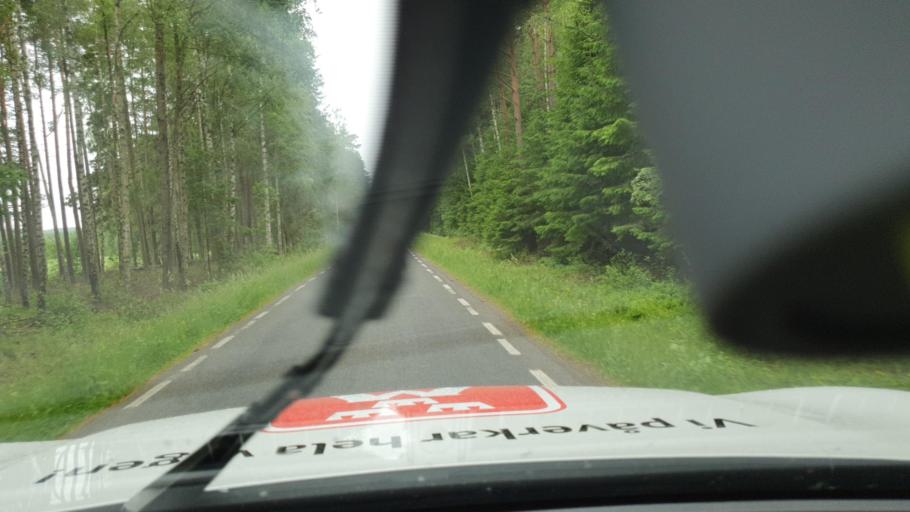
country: SE
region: Vaestra Goetaland
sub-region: Tibro Kommun
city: Tibro
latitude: 58.3320
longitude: 14.1931
